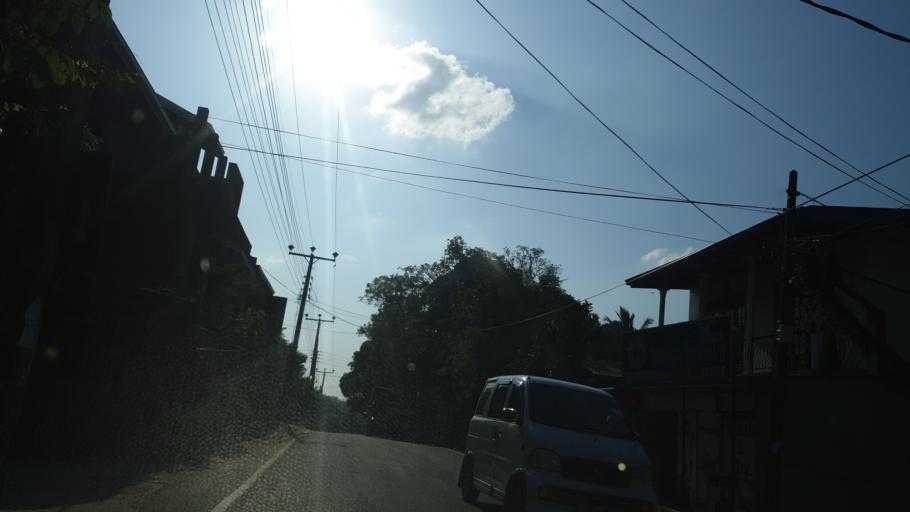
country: LK
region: Western
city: Battaramulla South
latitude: 6.8809
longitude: 79.9365
